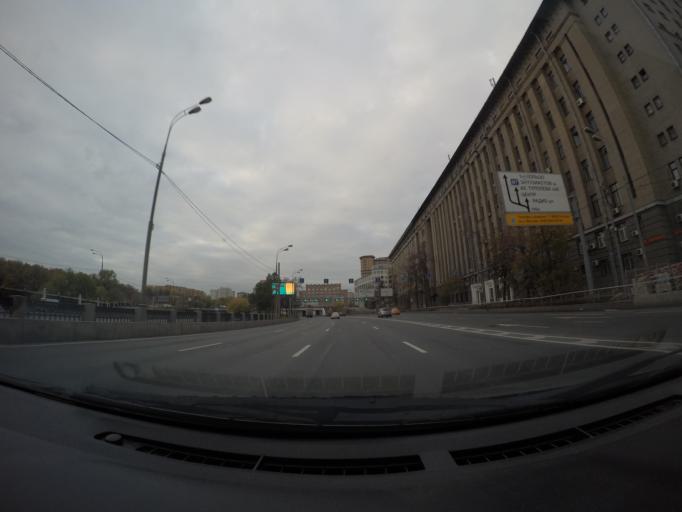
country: RU
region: Moscow
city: Lefortovo
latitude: 55.7713
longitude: 37.6776
